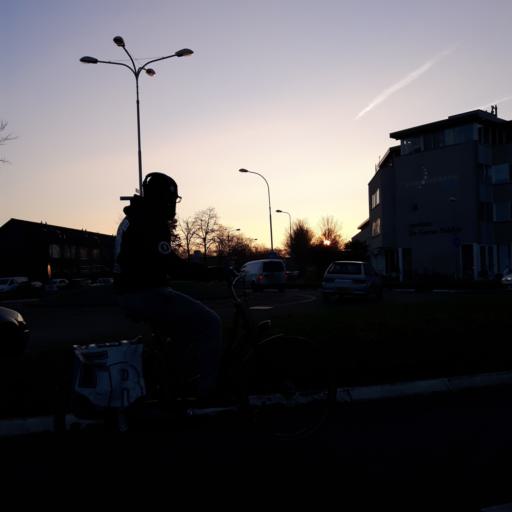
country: NL
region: Zeeland
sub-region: Gemeente Goes
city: Goes
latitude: 51.5124
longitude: 3.8815
